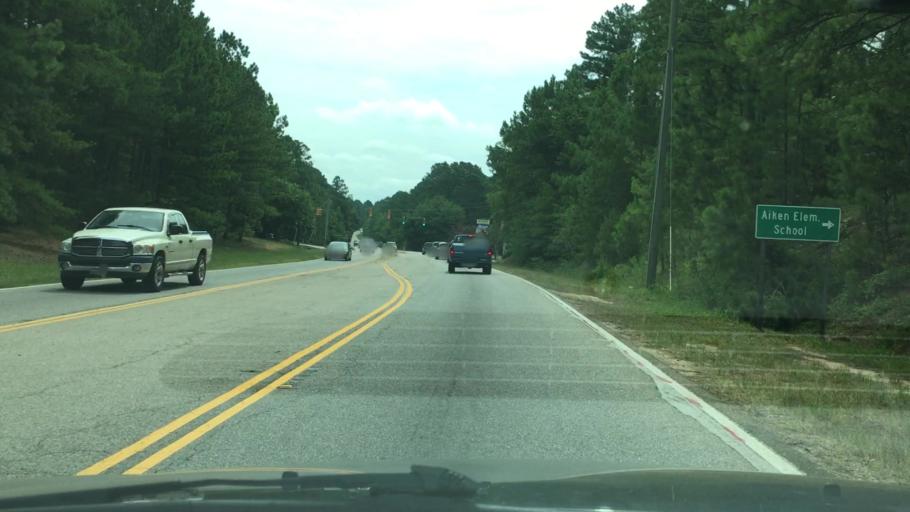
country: US
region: South Carolina
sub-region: Aiken County
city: Warrenville
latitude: 33.5295
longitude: -81.7638
